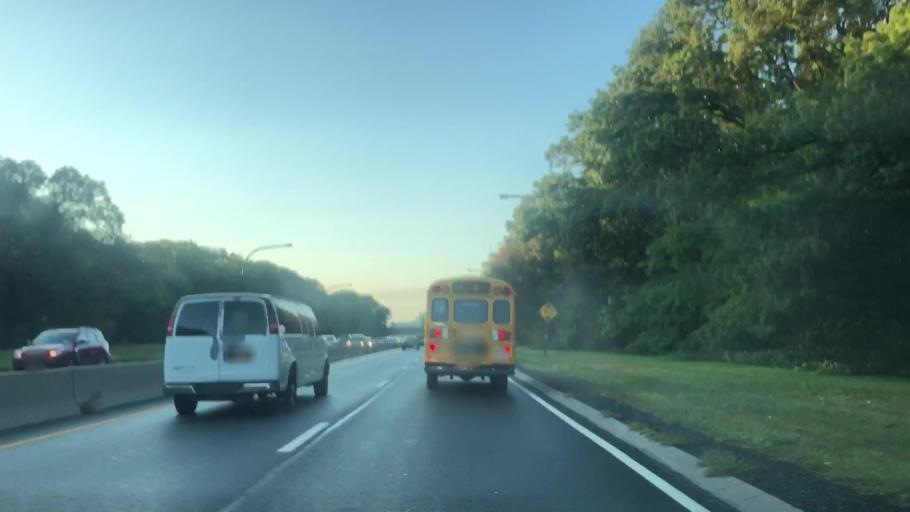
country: US
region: New York
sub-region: Nassau County
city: Salisbury
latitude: 40.7511
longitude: -73.5485
